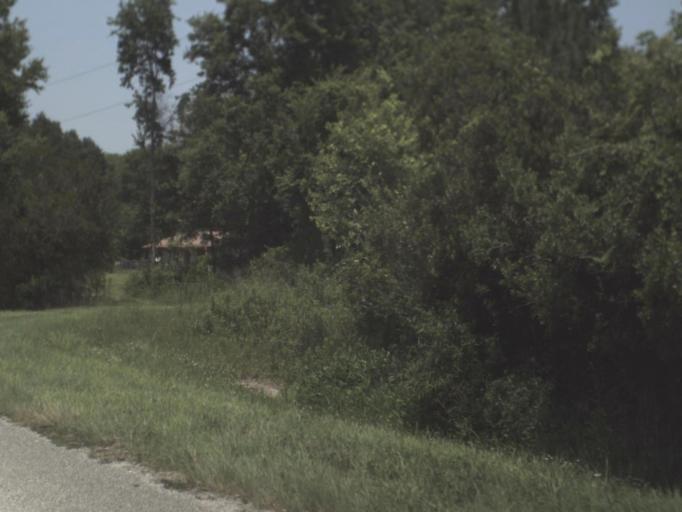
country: US
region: Florida
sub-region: Bradford County
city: Starke
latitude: 30.0620
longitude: -82.0659
